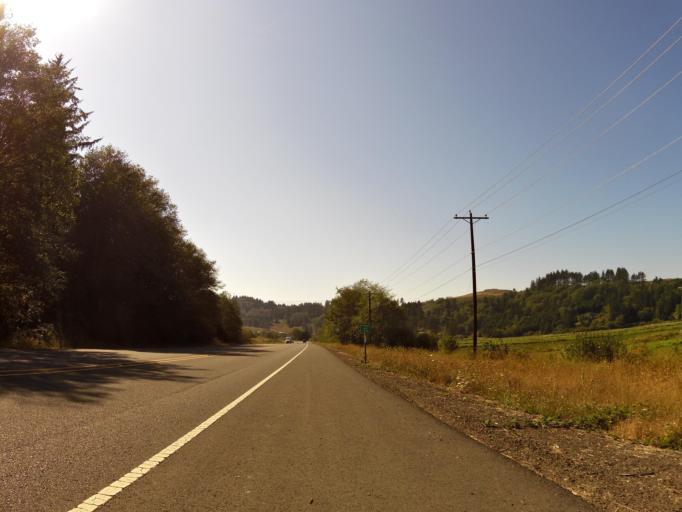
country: US
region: Oregon
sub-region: Tillamook County
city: Pacific City
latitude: 45.1602
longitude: -123.9420
